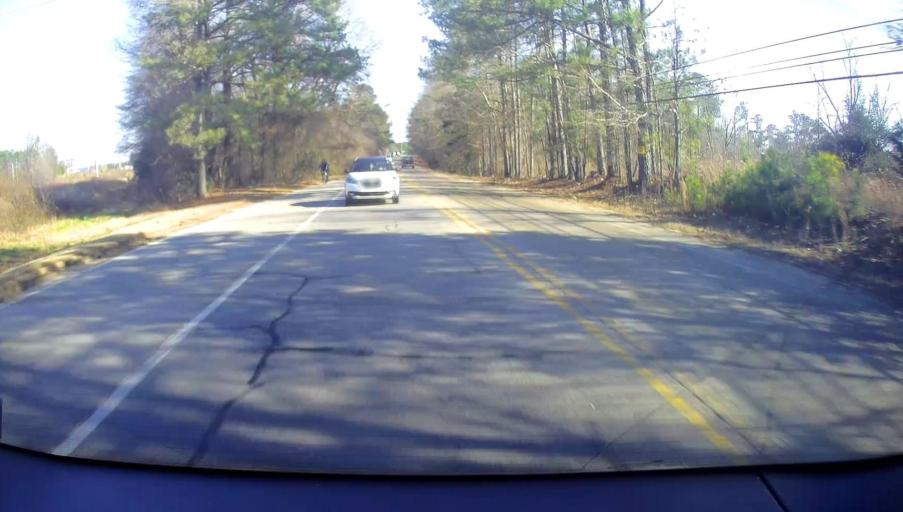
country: US
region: Georgia
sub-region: Butts County
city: Jackson
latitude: 33.2841
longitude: -83.9305
